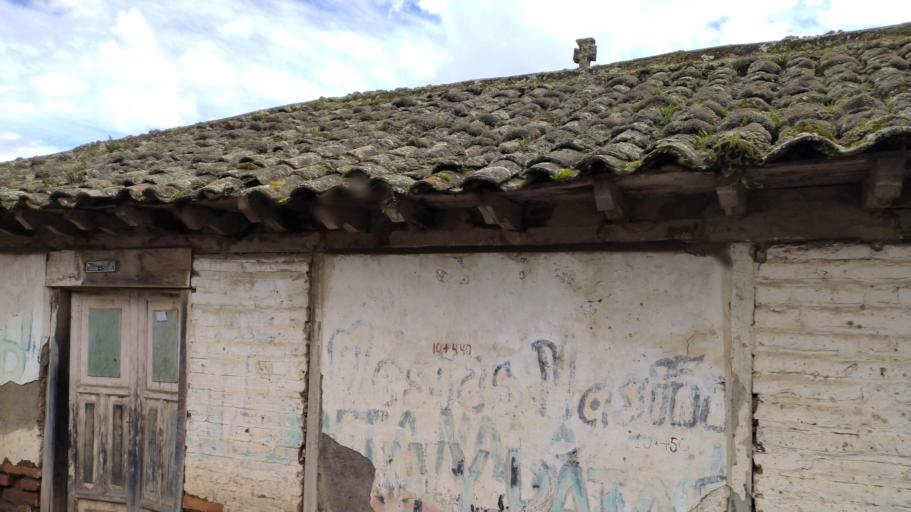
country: EC
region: Chimborazo
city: Riobamba
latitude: -1.6777
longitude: -78.5731
